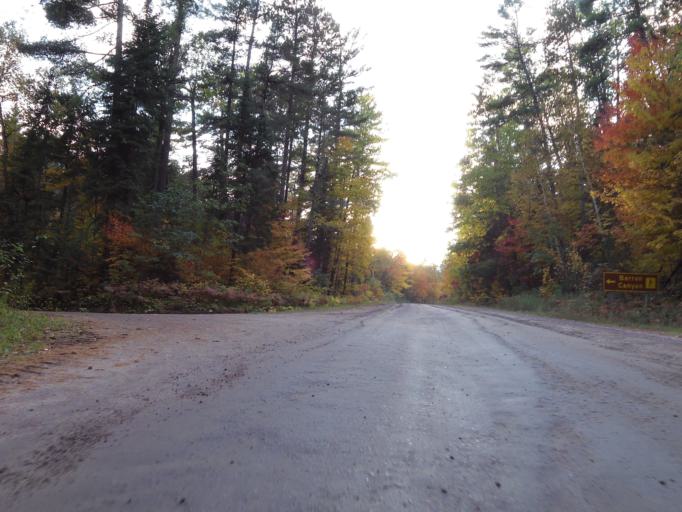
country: CA
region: Ontario
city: Deep River
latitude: 45.8901
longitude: -77.6347
